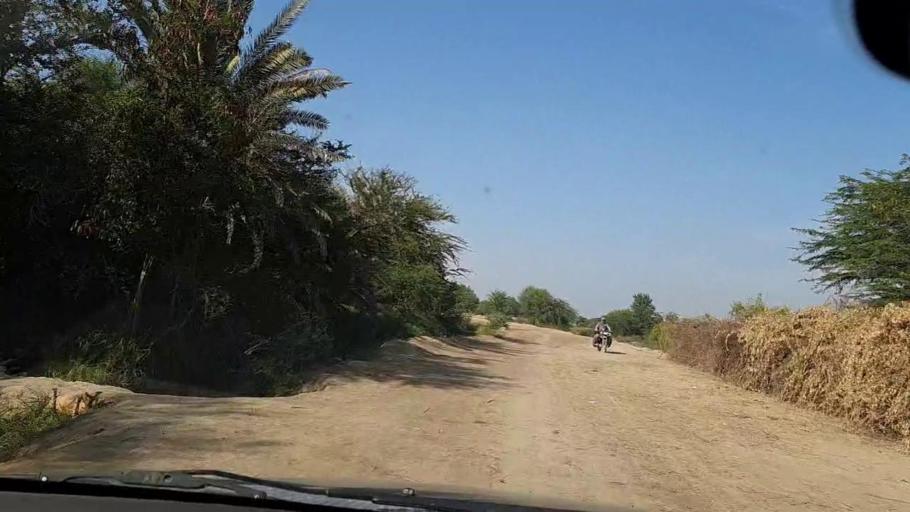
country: PK
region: Sindh
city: Mirpur Batoro
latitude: 24.6529
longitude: 68.2542
